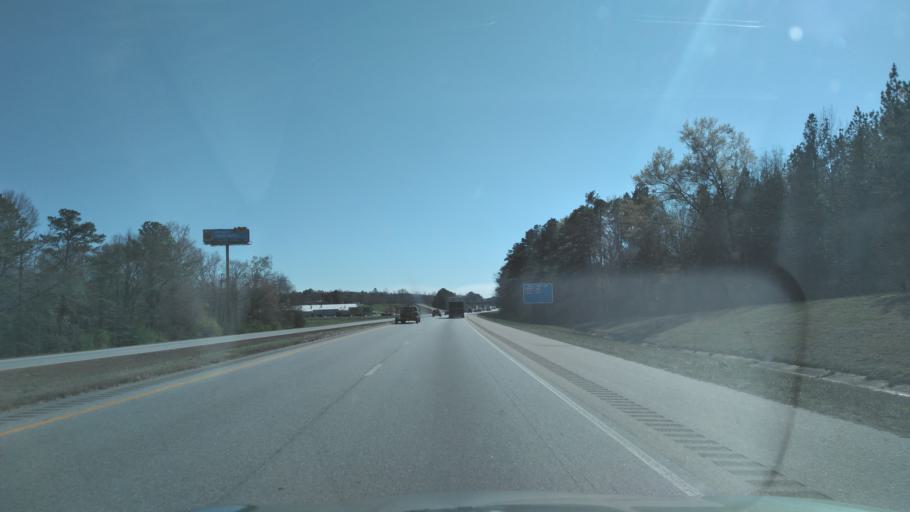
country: US
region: Alabama
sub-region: Lowndes County
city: Fort Deposit
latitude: 31.9927
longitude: -86.5264
